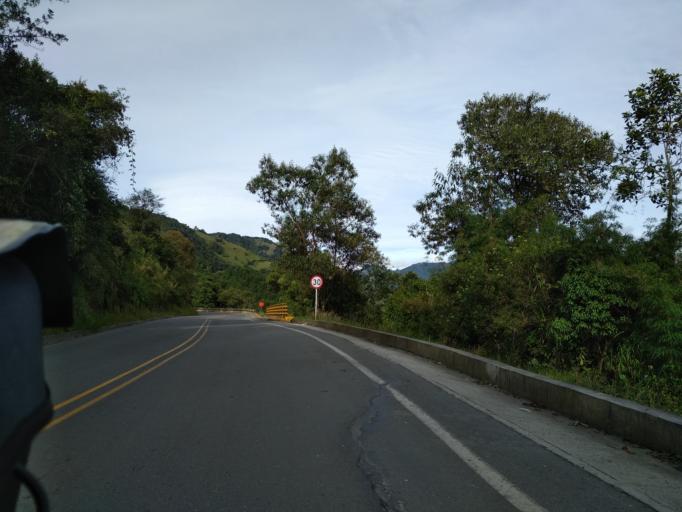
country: CO
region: Tolima
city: Herveo
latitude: 5.1304
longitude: -75.2001
